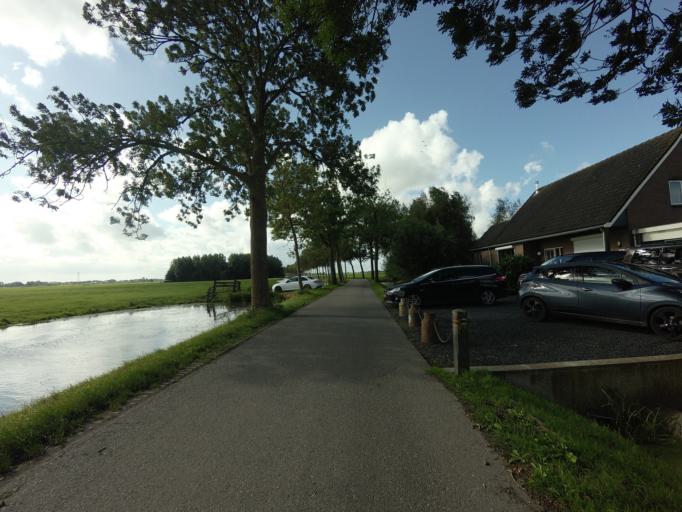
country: NL
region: North Holland
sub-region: Gemeente Hoorn
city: Hoorn
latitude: 52.6697
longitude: 5.0039
